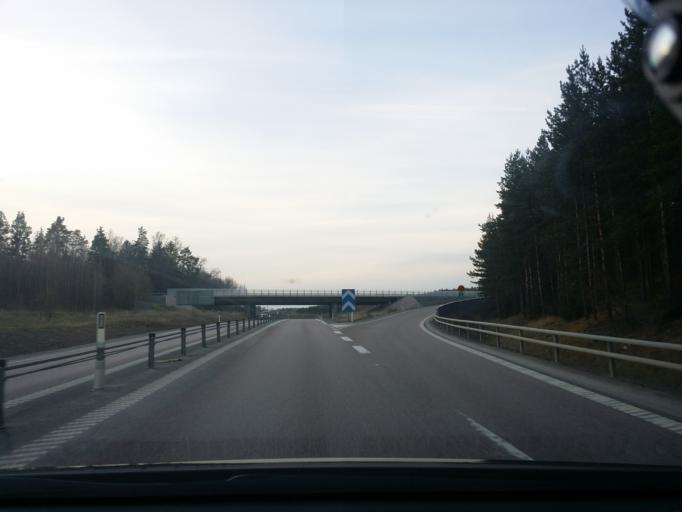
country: SE
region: Uppsala
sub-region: Enkopings Kommun
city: Enkoping
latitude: 59.6433
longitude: 17.0534
